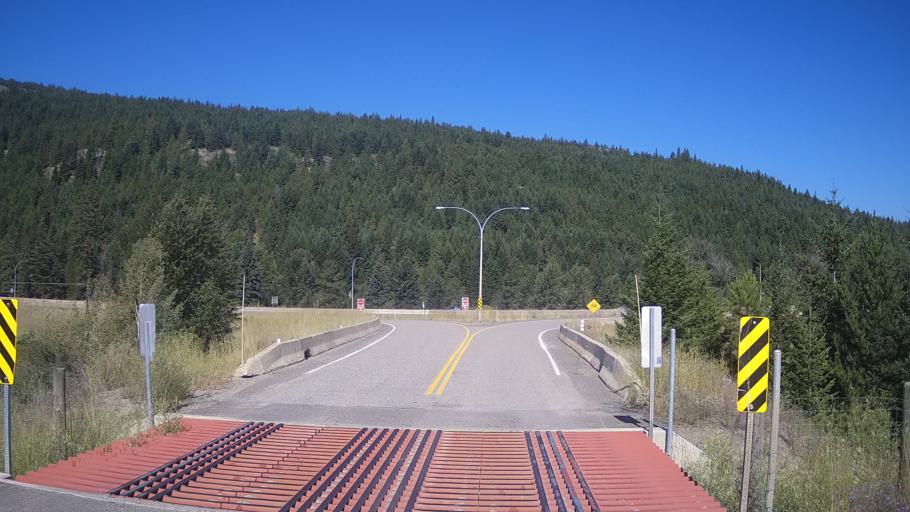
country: CA
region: British Columbia
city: Merritt
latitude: 49.8808
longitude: -120.9025
